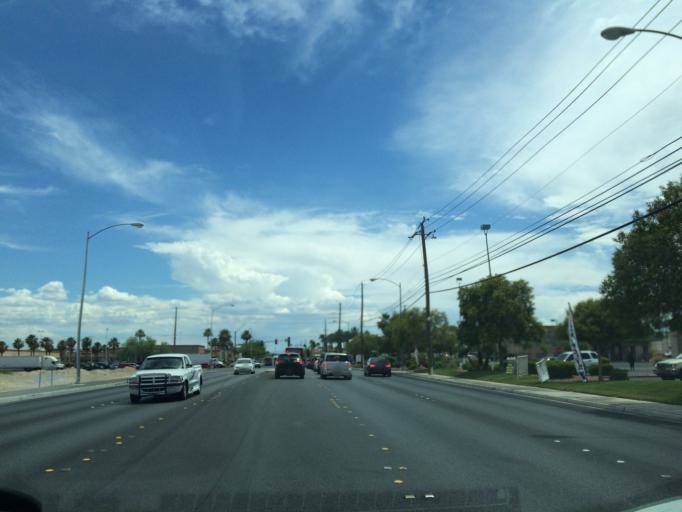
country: US
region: Nevada
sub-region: Clark County
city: North Las Vegas
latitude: 36.2411
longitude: -115.1711
